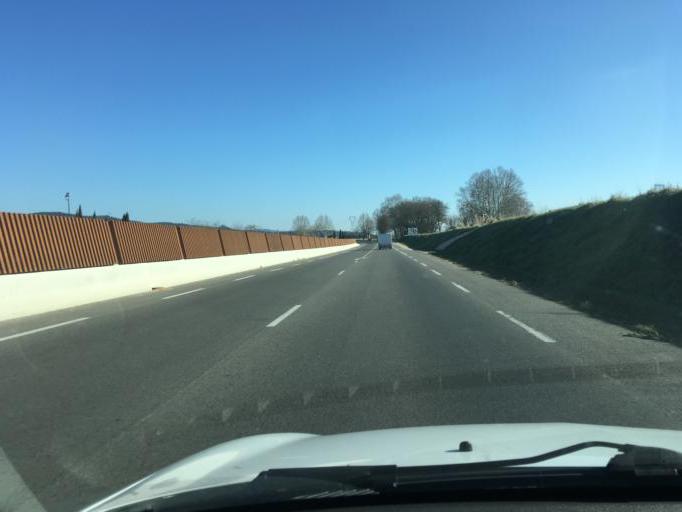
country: FR
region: Provence-Alpes-Cote d'Azur
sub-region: Departement du Vaucluse
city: Villelaure
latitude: 43.7085
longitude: 5.4261
